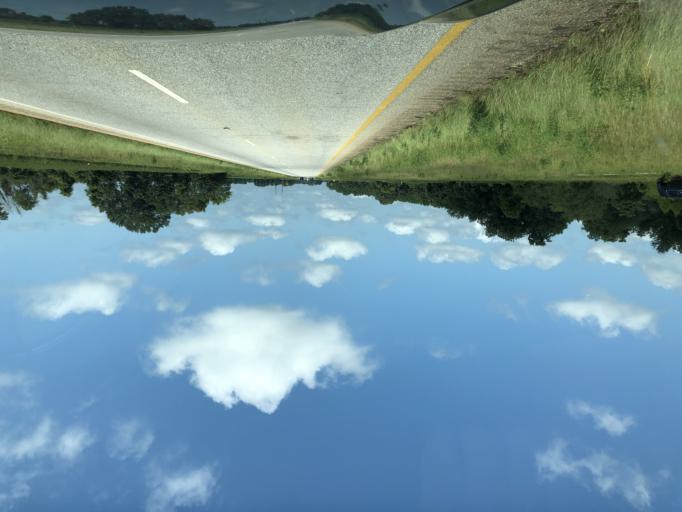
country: US
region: Alabama
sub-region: Henry County
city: Abbeville
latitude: 31.6001
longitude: -85.2770
